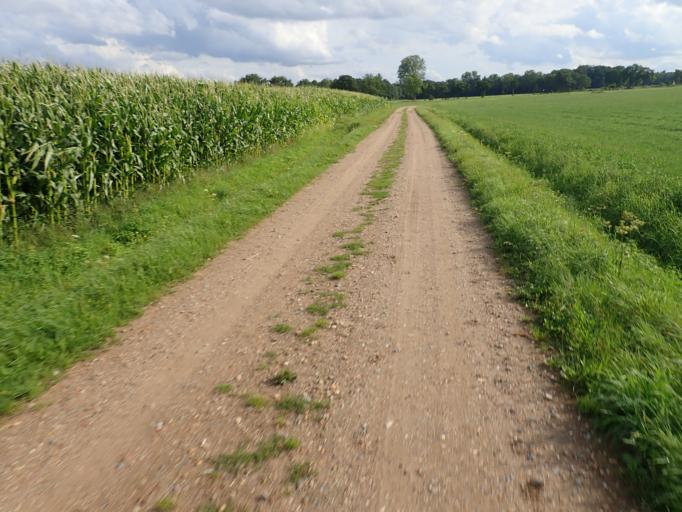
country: BE
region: Flanders
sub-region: Provincie Antwerpen
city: Zoersel
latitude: 51.2532
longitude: 4.7160
